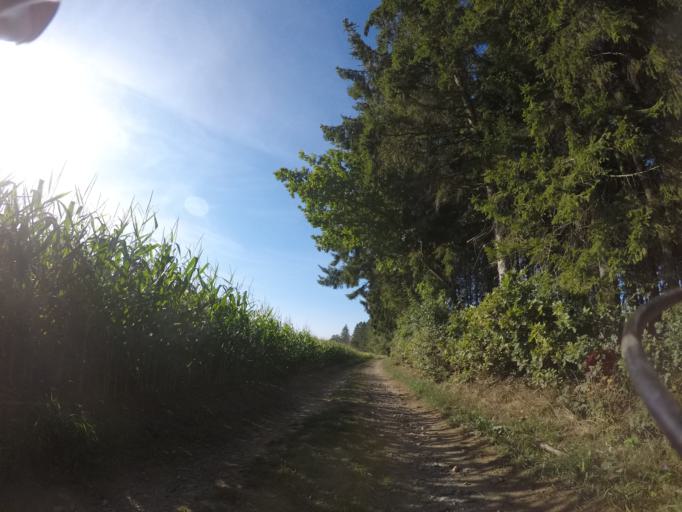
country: BE
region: Wallonia
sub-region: Province du Luxembourg
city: Fauvillers
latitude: 49.9209
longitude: 5.6582
